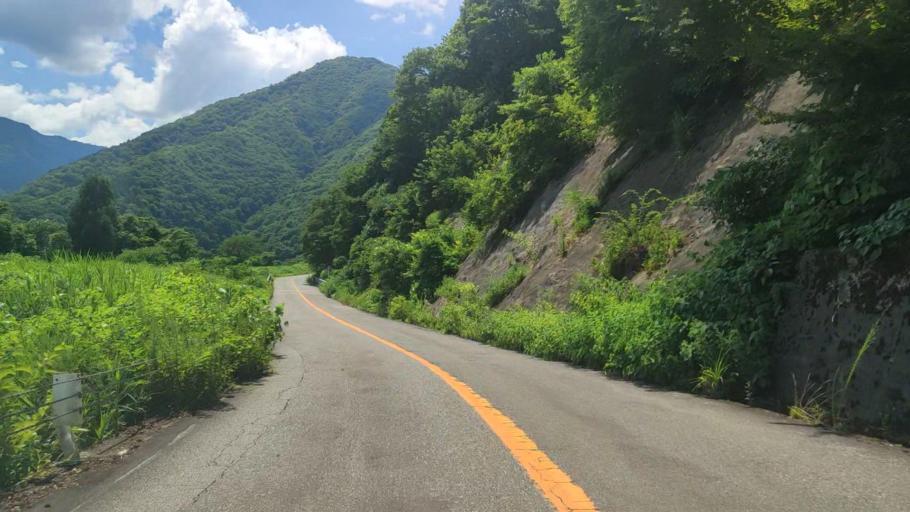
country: JP
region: Fukui
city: Ono
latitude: 35.9075
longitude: 136.5313
